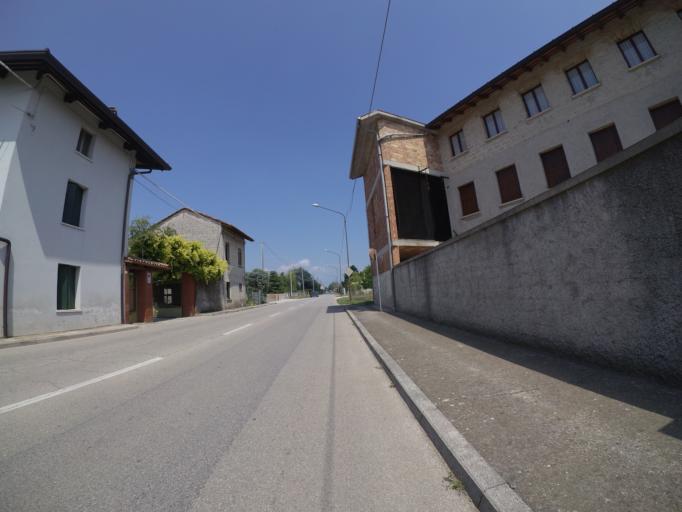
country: IT
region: Friuli Venezia Giulia
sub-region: Provincia di Udine
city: Sedegliano
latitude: 45.9910
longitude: 12.9687
